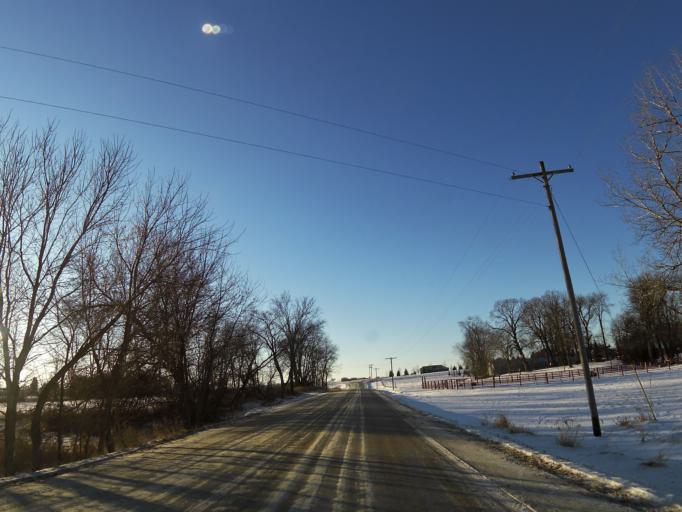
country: US
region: Minnesota
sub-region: Le Sueur County
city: New Prague
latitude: 44.6331
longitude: -93.5169
